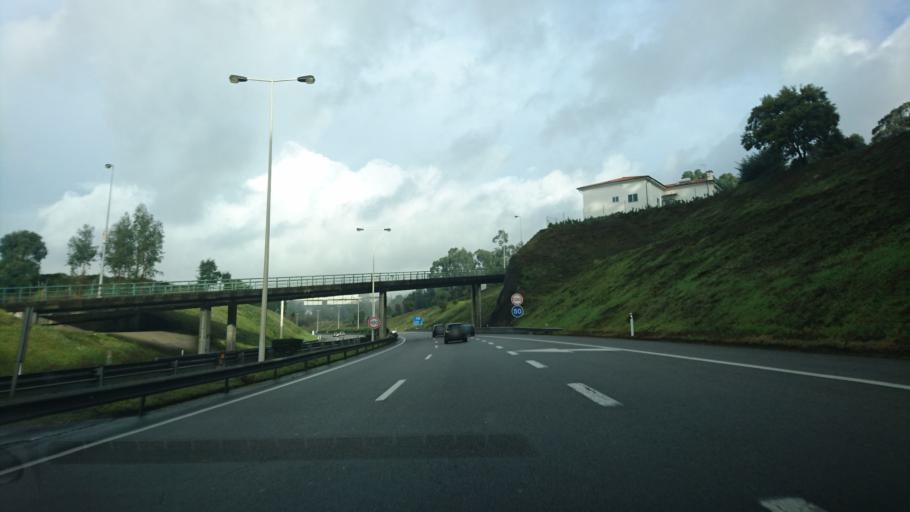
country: PT
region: Porto
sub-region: Gondomar
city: Gondomar
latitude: 41.1513
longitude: -8.5484
